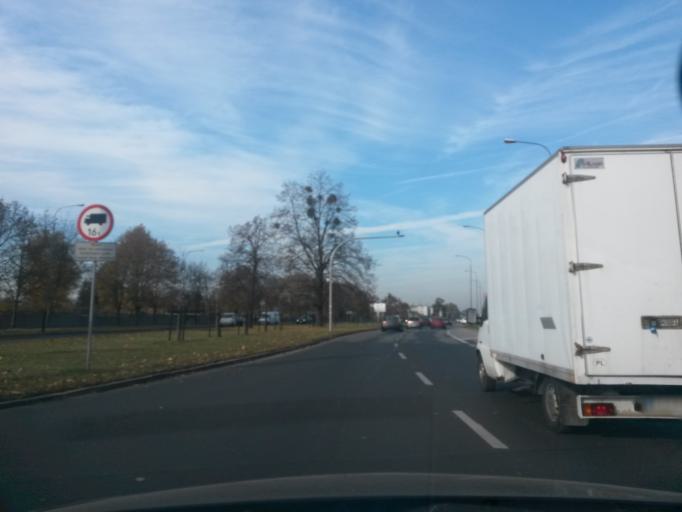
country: PL
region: Greater Poland Voivodeship
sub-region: Poznan
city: Poznan
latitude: 52.3932
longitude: 16.8861
